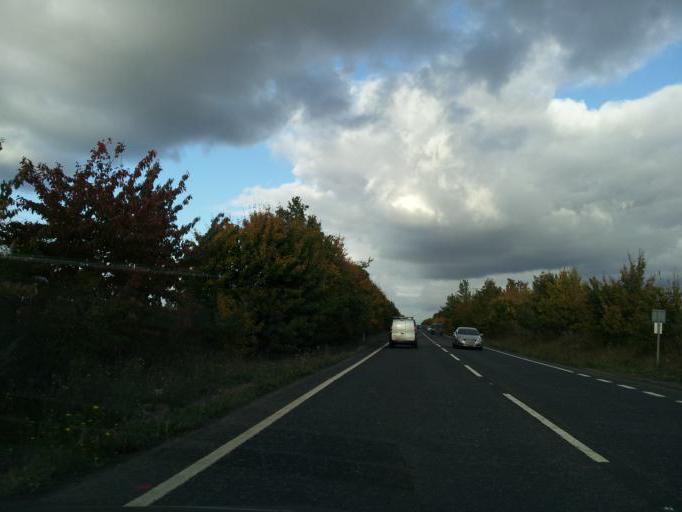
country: GB
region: England
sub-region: Cambridgeshire
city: Saint Neots
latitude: 52.2162
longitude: -0.2453
